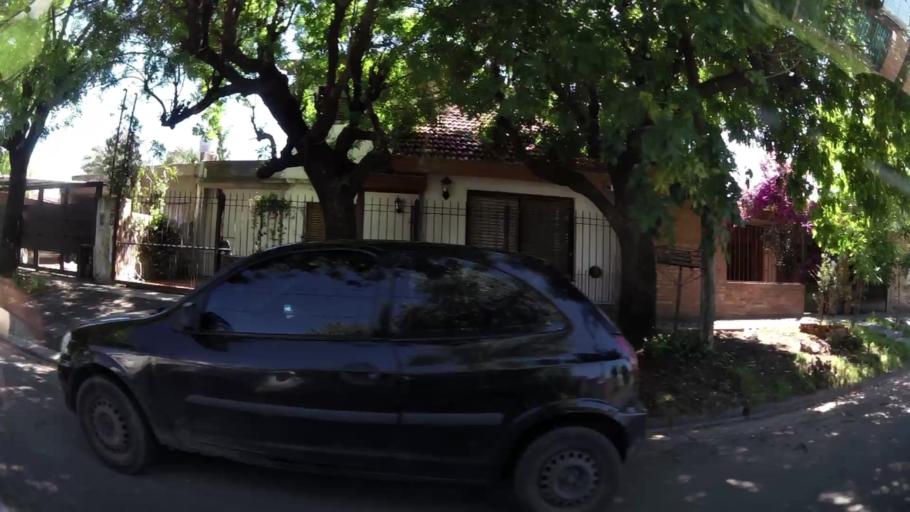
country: AR
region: Buenos Aires
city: Ituzaingo
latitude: -34.6634
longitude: -58.6527
